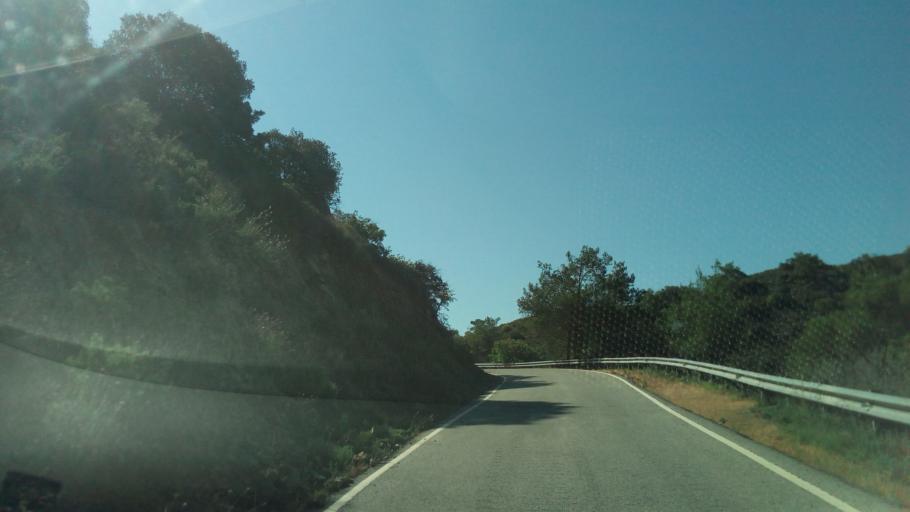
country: CY
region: Lefkosia
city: Lythrodontas
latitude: 34.8824
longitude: 33.2058
